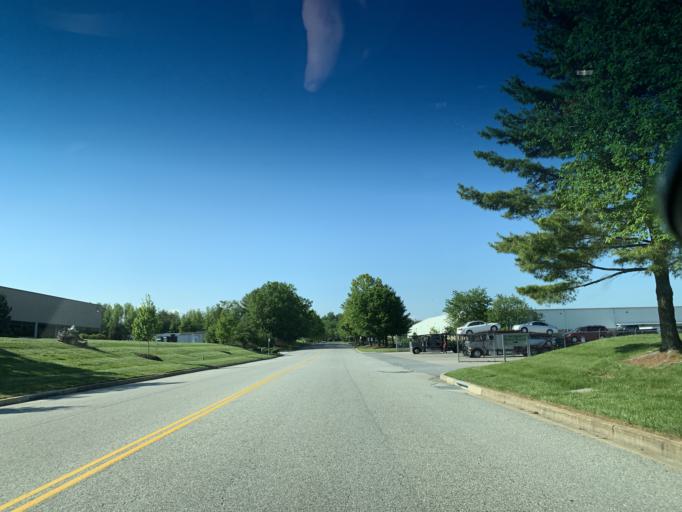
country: US
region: Maryland
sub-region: Harford County
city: Riverside
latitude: 39.4802
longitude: -76.2349
